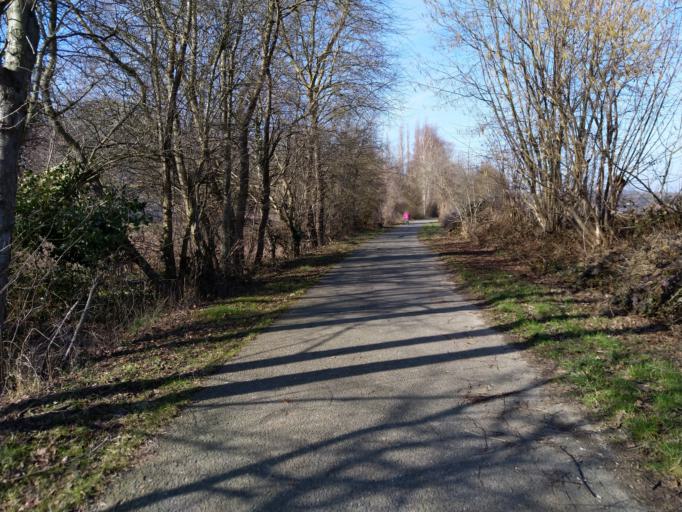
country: BE
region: Wallonia
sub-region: Province du Hainaut
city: Chasse Royale
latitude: 50.4260
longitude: 3.9232
